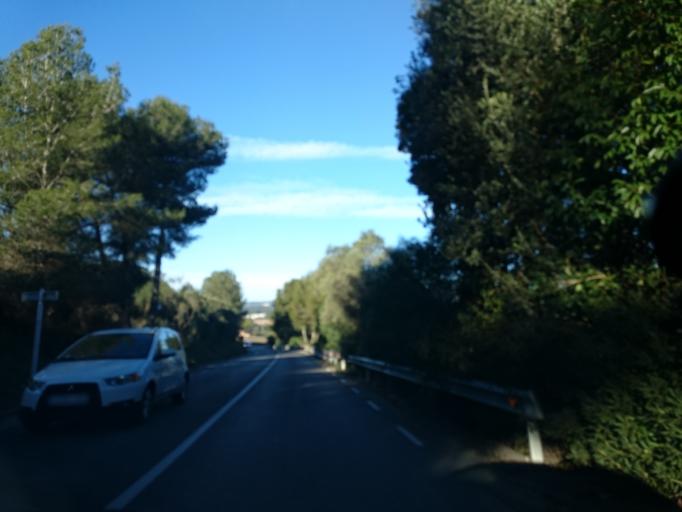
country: ES
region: Catalonia
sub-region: Provincia de Barcelona
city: Sitges
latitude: 41.2450
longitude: 1.7931
